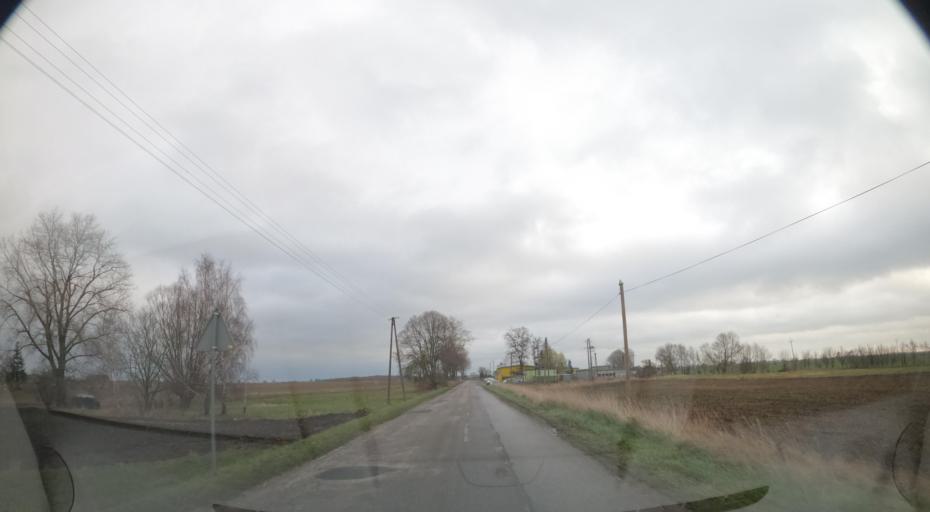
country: PL
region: Greater Poland Voivodeship
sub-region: Powiat pilski
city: Lobzenica
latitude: 53.2678
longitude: 17.2020
